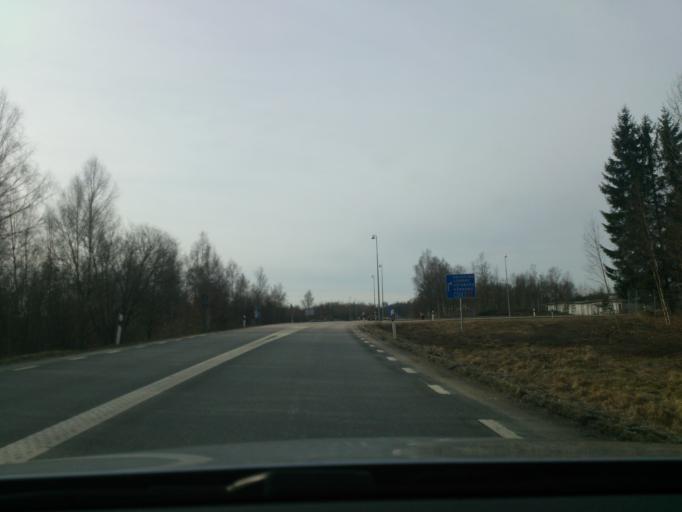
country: SE
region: Kronoberg
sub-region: Alvesta Kommun
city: Alvesta
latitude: 56.9241
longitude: 14.5593
